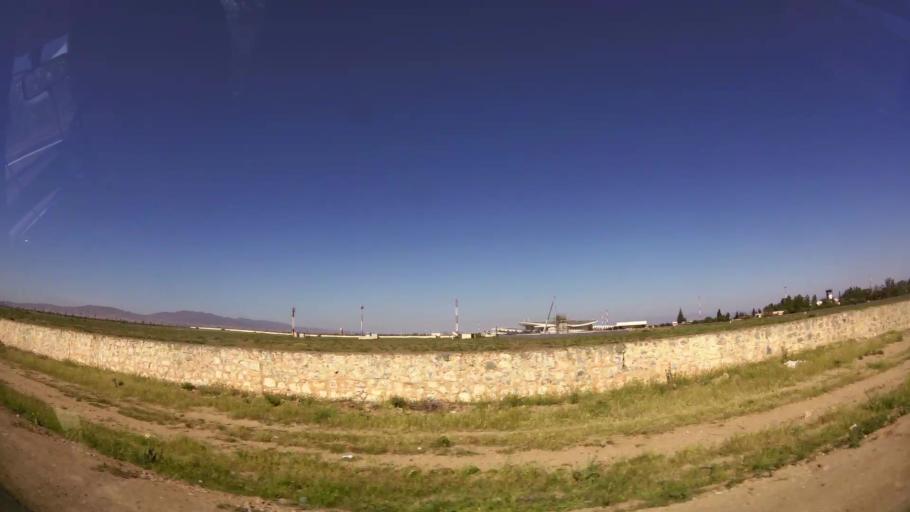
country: MA
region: Oriental
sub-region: Oujda-Angad
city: Oujda
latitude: 34.7856
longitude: -1.9491
